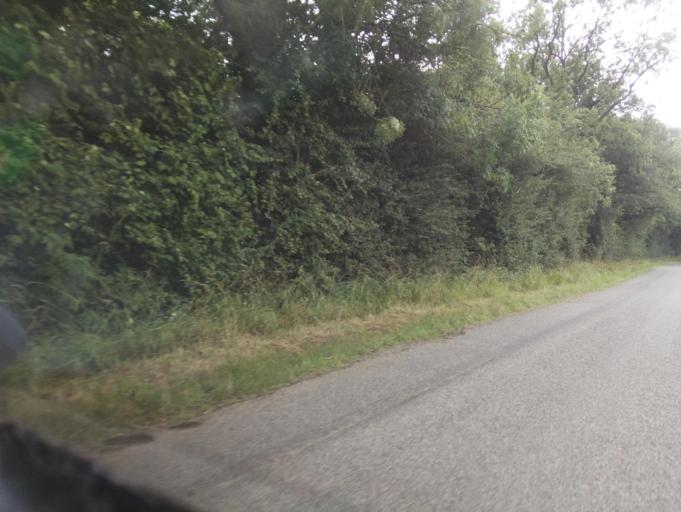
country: GB
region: England
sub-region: Northamptonshire
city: Corby
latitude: 52.5221
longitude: -0.6298
